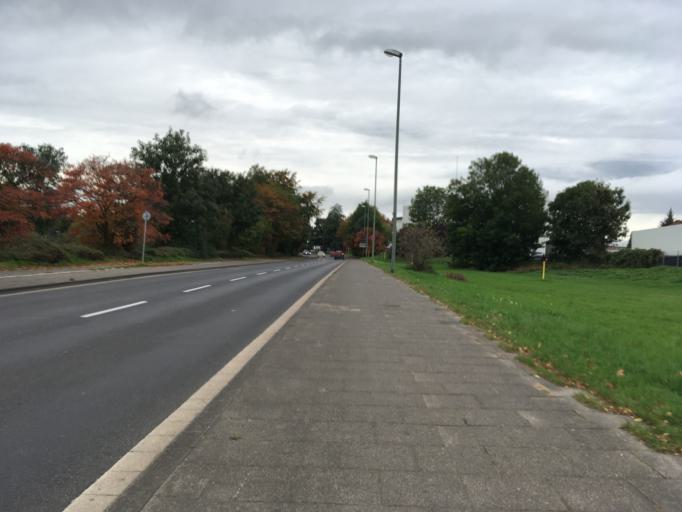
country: DE
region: North Rhine-Westphalia
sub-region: Regierungsbezirk Dusseldorf
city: Neuss
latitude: 51.2024
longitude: 6.7081
